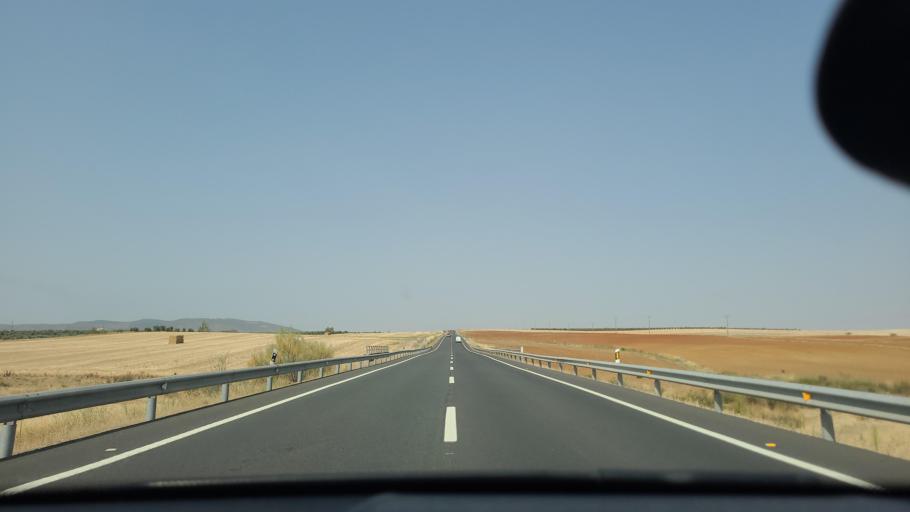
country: ES
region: Extremadura
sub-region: Provincia de Badajoz
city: Ahillones
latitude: 38.2542
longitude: -5.9119
